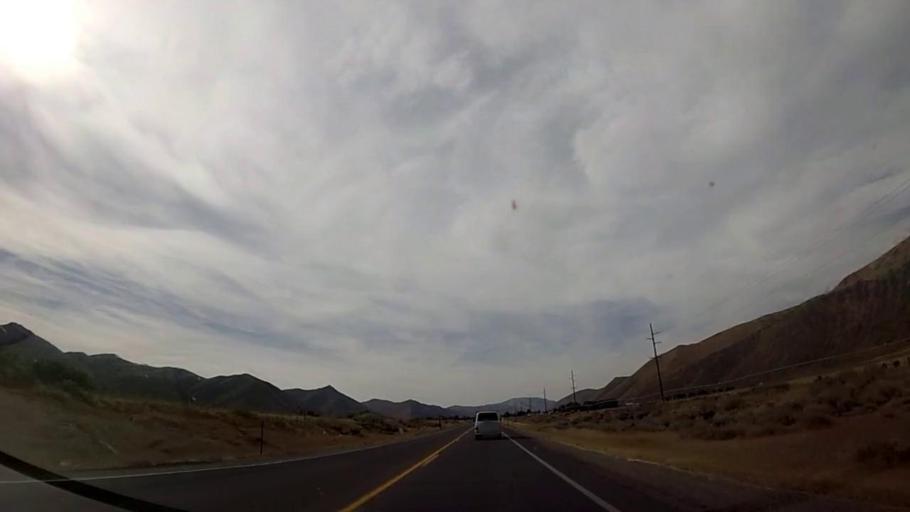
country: US
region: Idaho
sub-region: Blaine County
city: Bellevue
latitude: 43.4777
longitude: -114.2685
